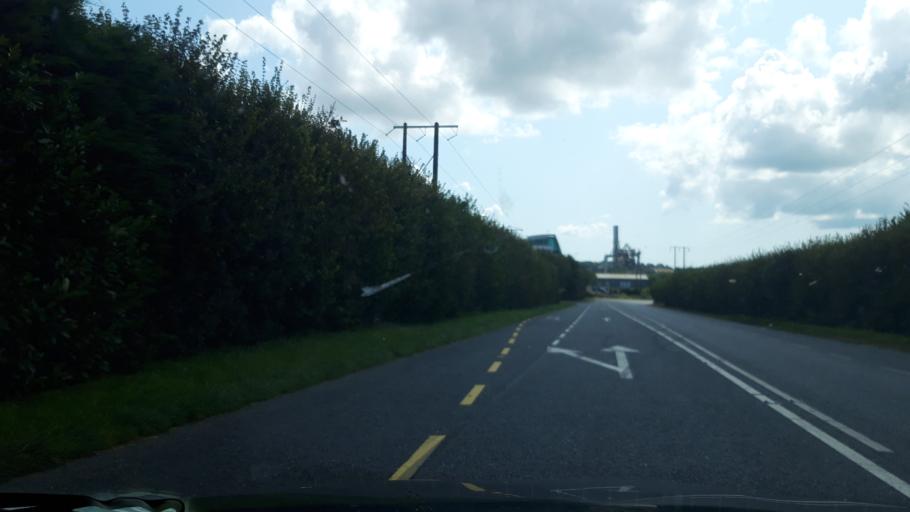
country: IE
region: Munster
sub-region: Waterford
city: Waterford
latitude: 52.2682
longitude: -7.0405
